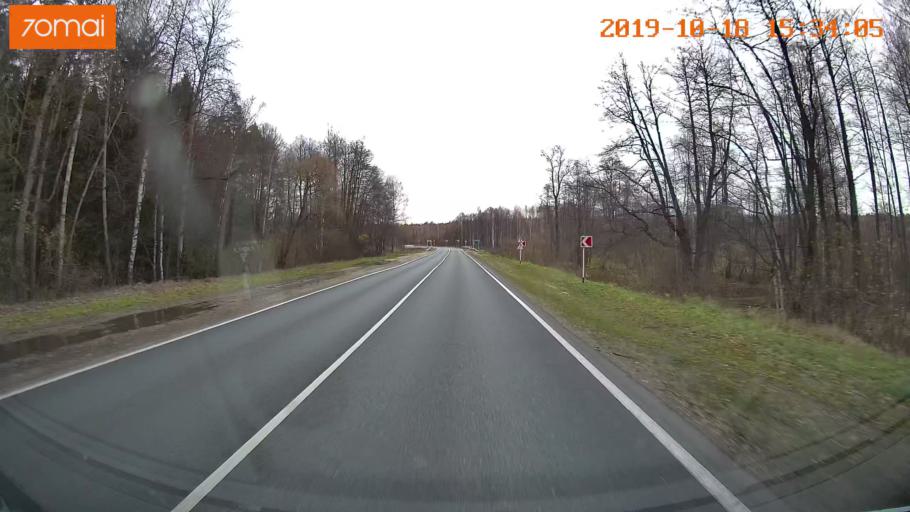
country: RU
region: Vladimir
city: Anopino
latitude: 55.8502
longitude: 40.6451
